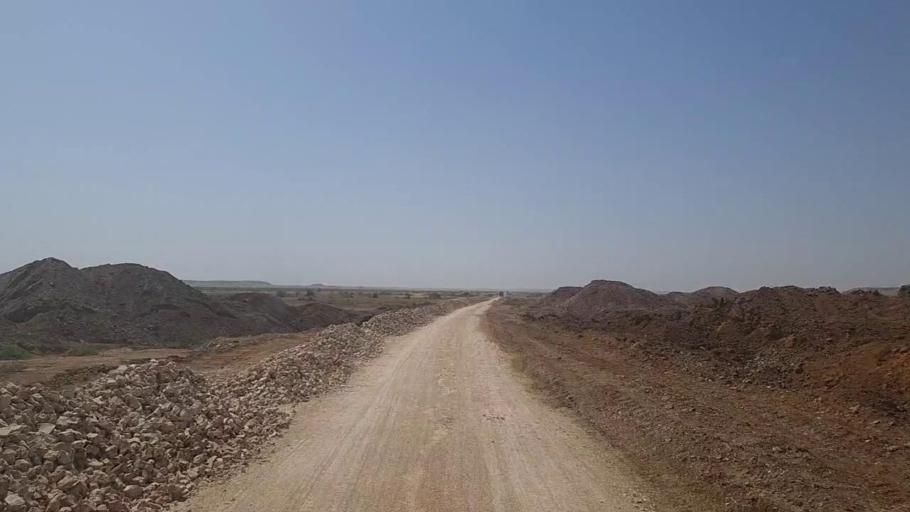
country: PK
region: Sindh
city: Kotri
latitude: 25.1468
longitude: 68.1888
